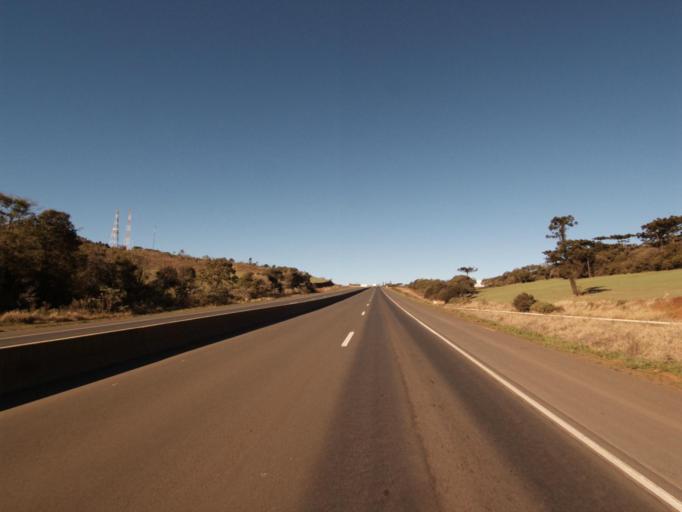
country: BR
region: Santa Catarina
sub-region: Xanxere
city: Xanxere
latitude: -26.8858
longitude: -52.4289
